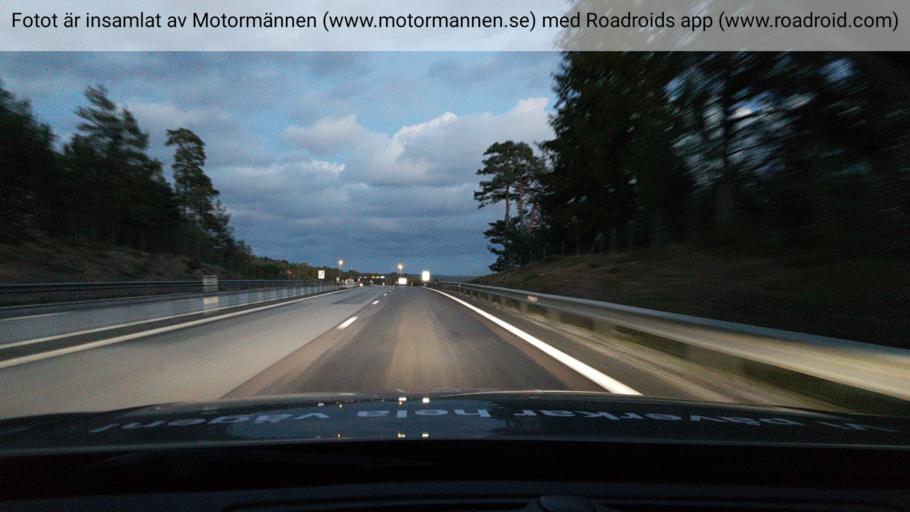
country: SE
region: Vaermland
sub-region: Kristinehamns Kommun
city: Kristinehamn
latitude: 59.3761
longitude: 13.9267
